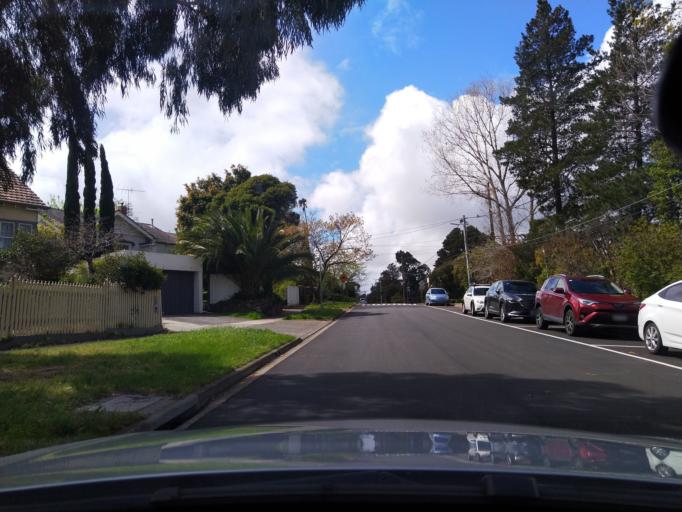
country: AU
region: Victoria
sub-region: Banyule
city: Bellfield
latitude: -37.7642
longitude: 145.0527
